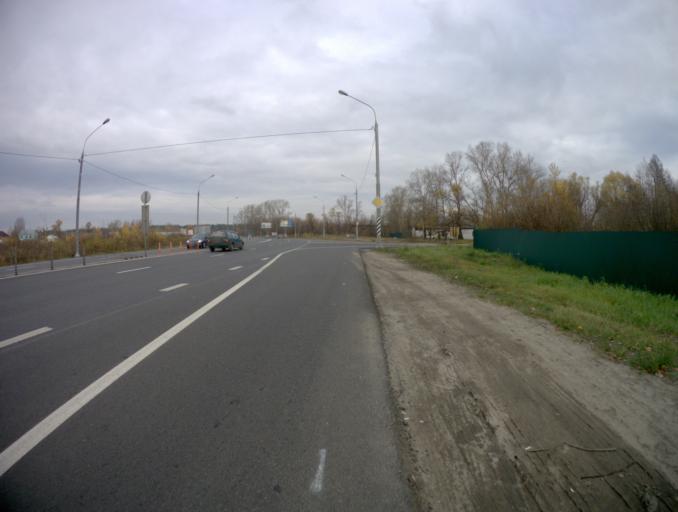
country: RU
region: Moskovskaya
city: Orekhovo-Zuyevo
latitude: 55.8396
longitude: 38.9704
